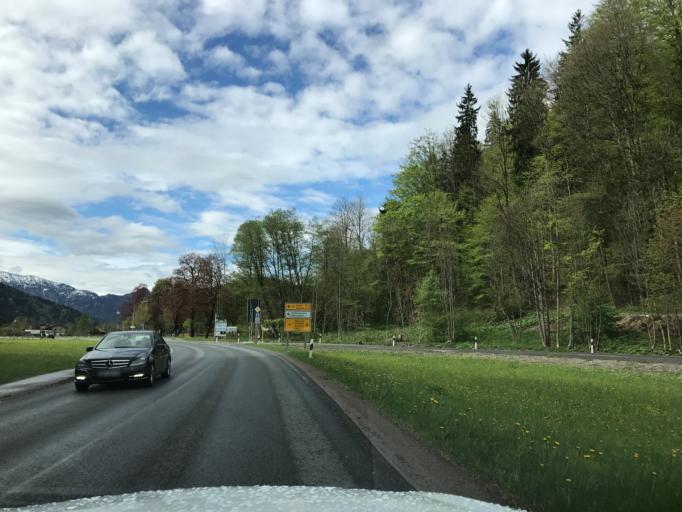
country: DE
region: Bavaria
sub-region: Upper Bavaria
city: Rottach-Egern
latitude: 47.6792
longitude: 11.7590
